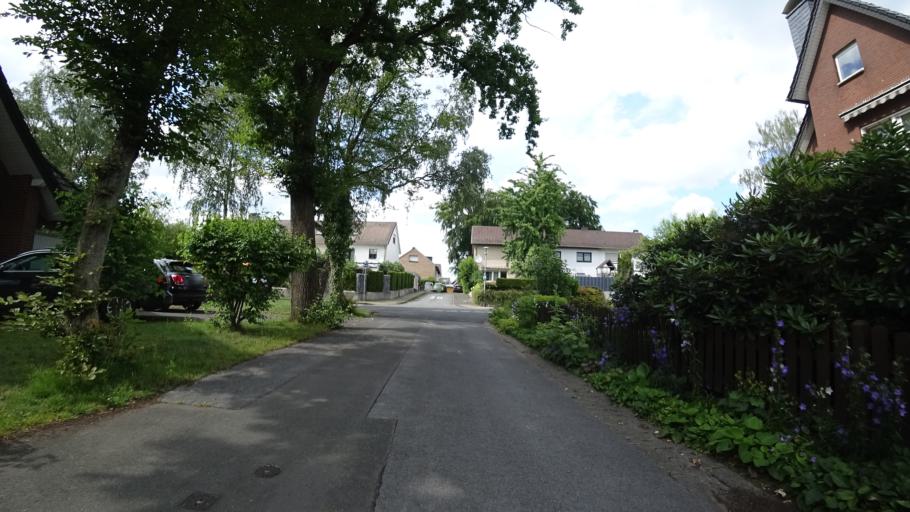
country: DE
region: North Rhine-Westphalia
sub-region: Regierungsbezirk Detmold
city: Guetersloh
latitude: 51.9279
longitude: 8.3779
